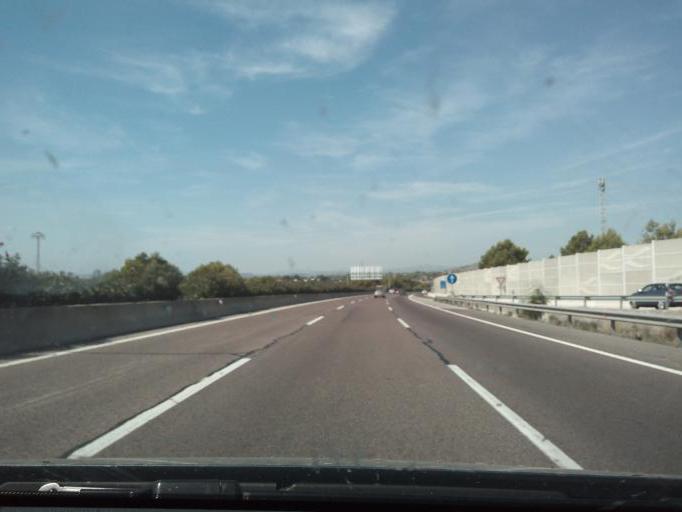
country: ES
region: Valencia
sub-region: Provincia de Valencia
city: Manises
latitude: 39.5150
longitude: -0.4848
